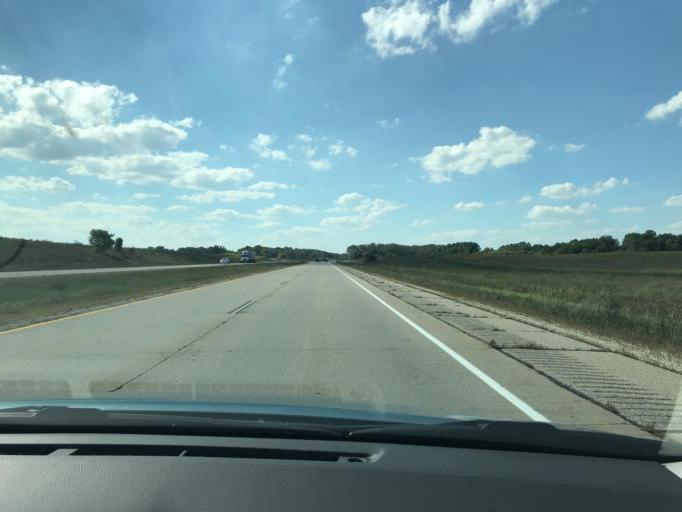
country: US
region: Wisconsin
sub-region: Kenosha County
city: Twin Lakes
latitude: 42.5812
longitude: -88.2474
